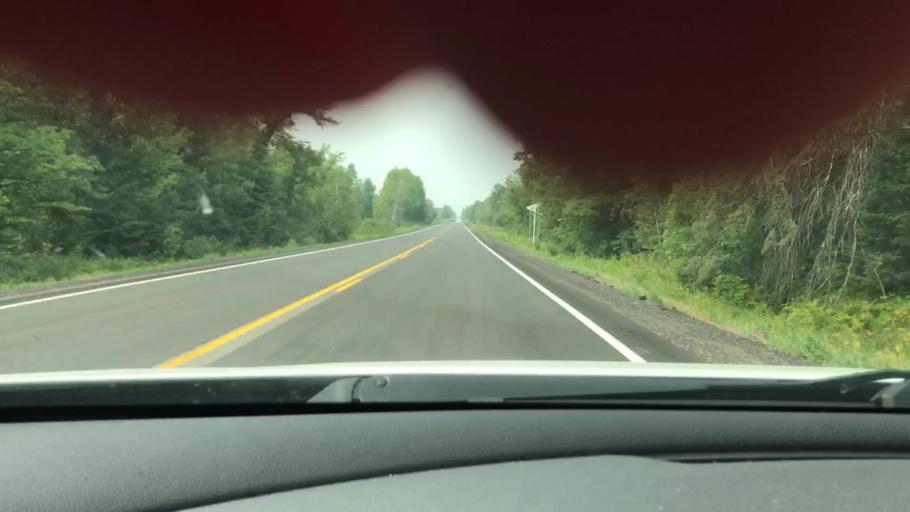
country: US
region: Minnesota
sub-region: Itasca County
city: Cohasset
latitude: 47.3607
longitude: -93.8634
